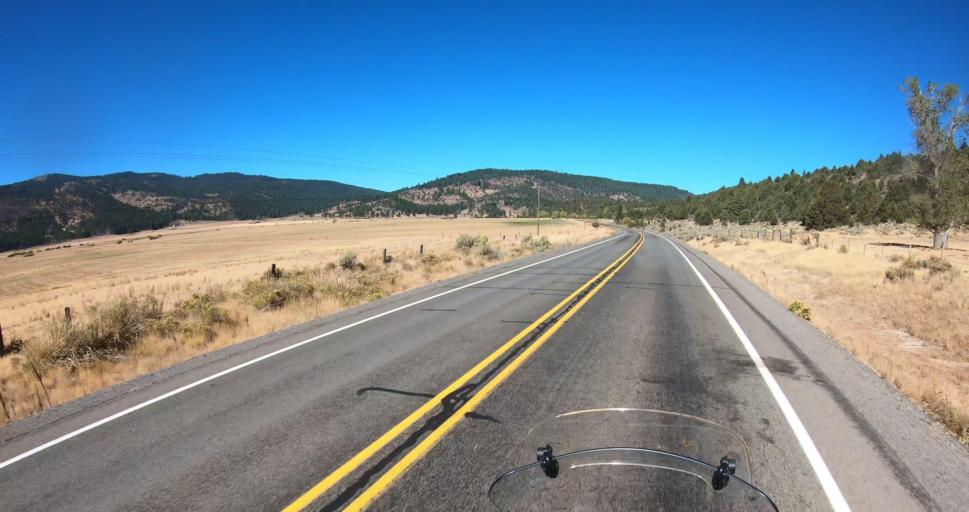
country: US
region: Oregon
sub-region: Lake County
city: Lakeview
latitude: 42.3730
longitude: -120.2976
